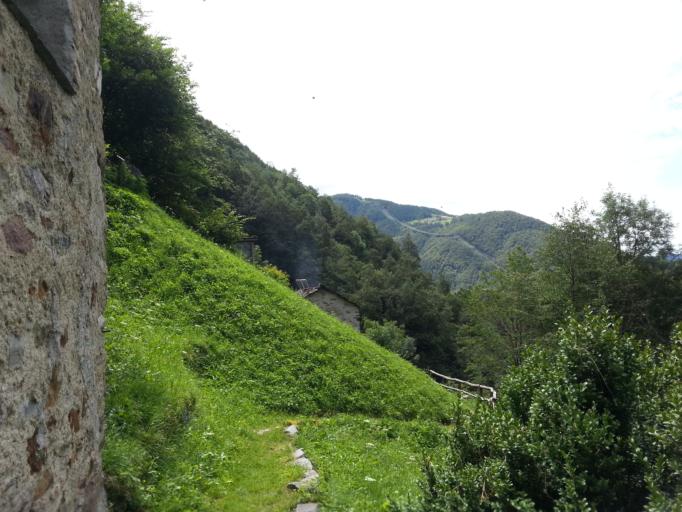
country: IT
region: Lombardy
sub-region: Provincia di Lecco
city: Pagnona
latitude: 46.0649
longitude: 9.4124
